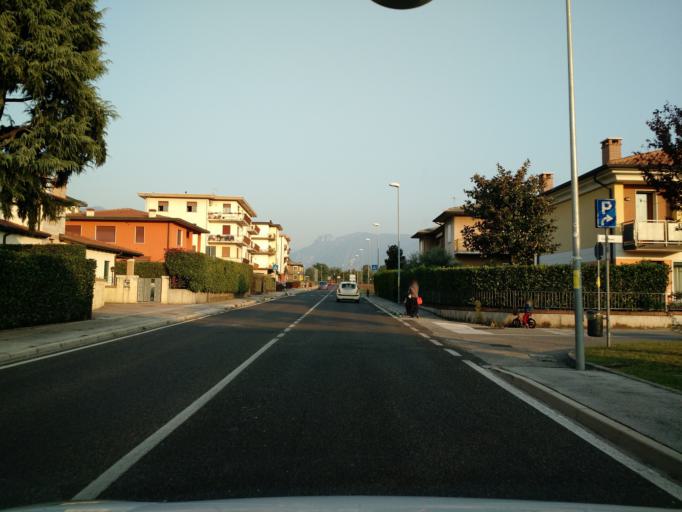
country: IT
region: Veneto
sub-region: Provincia di Vicenza
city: Grumolo Pedemonte
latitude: 45.7129
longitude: 11.4907
